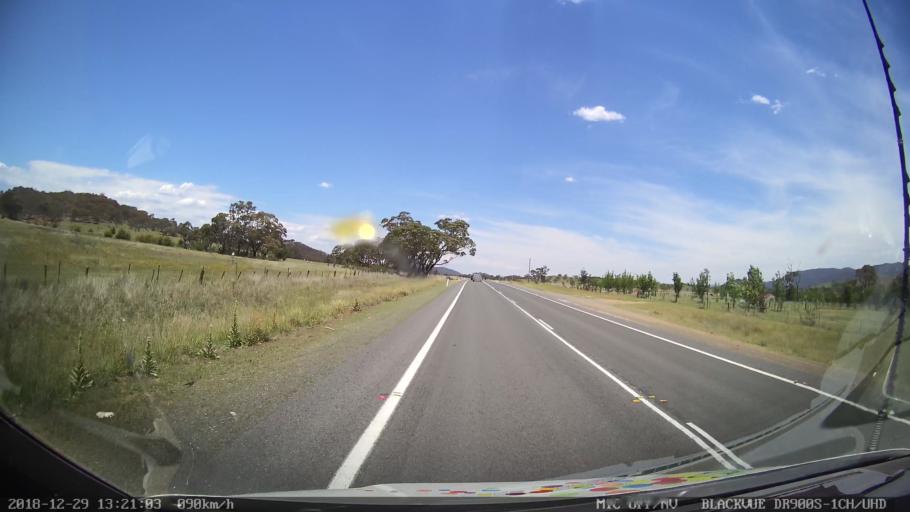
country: AU
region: Australian Capital Territory
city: Macarthur
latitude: -35.7870
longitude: 149.1630
